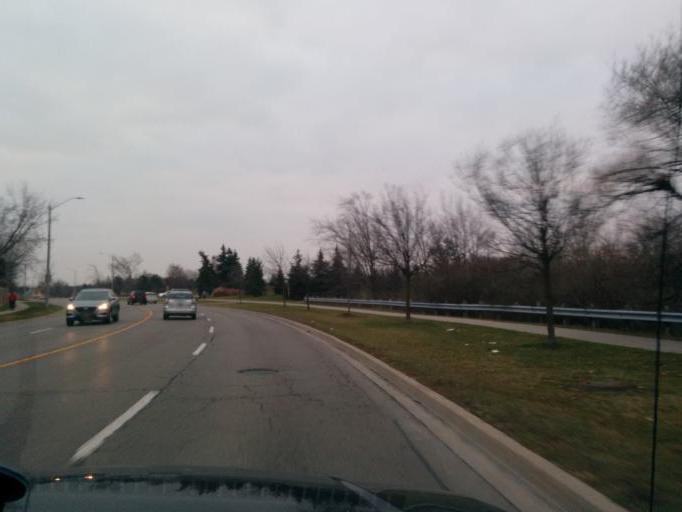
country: CA
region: Ontario
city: Etobicoke
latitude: 43.6212
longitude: -79.6126
